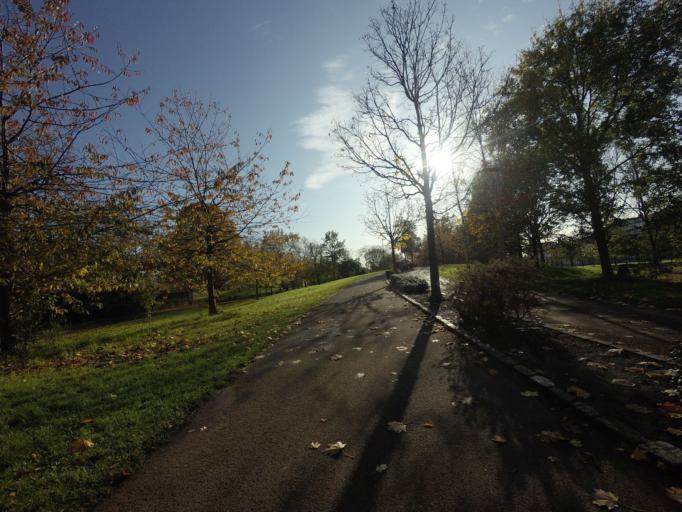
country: GB
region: England
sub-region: Greater London
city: Poplar
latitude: 51.5215
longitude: -0.0343
